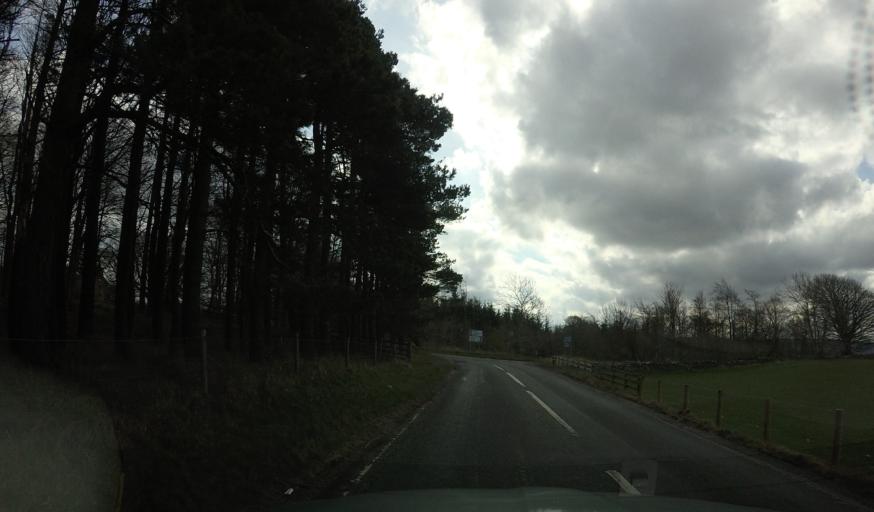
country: GB
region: Scotland
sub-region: Midlothian
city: Bonnyrigg
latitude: 55.7891
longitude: -3.1314
